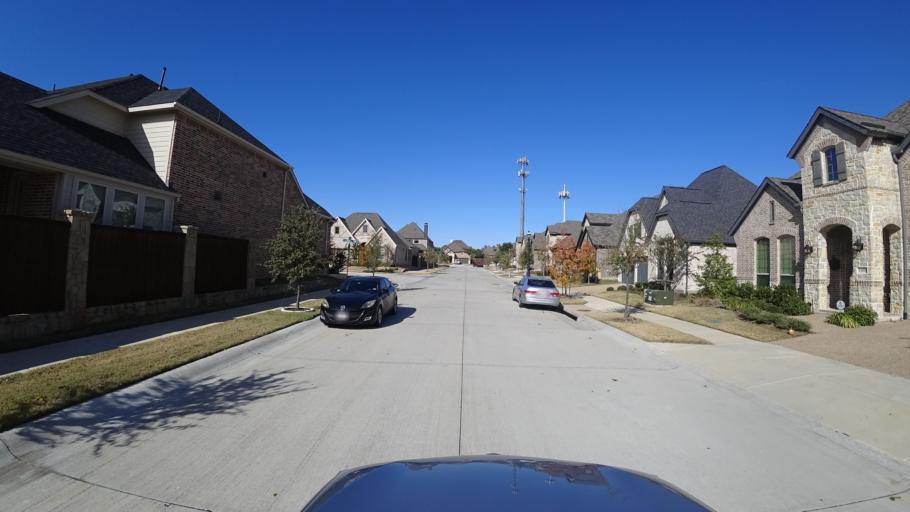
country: US
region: Texas
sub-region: Denton County
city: The Colony
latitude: 33.0257
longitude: -96.8953
